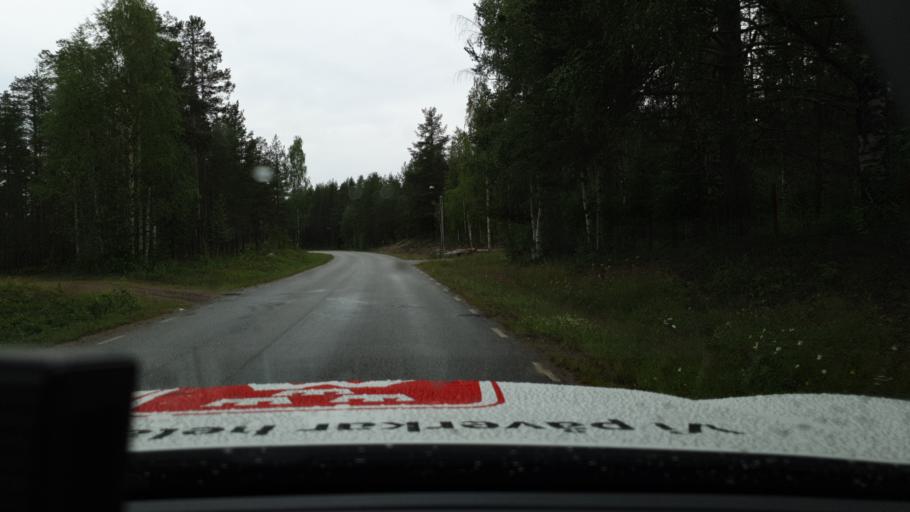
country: SE
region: Norrbotten
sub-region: Gallivare Kommun
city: Gaellivare
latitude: 66.4776
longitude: 20.8667
